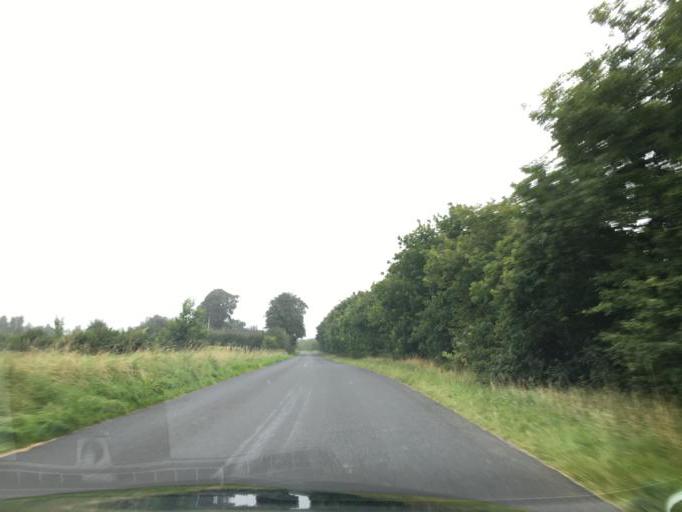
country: DK
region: South Denmark
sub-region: Kolding Kommune
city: Kolding
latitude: 55.5601
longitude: 9.4420
